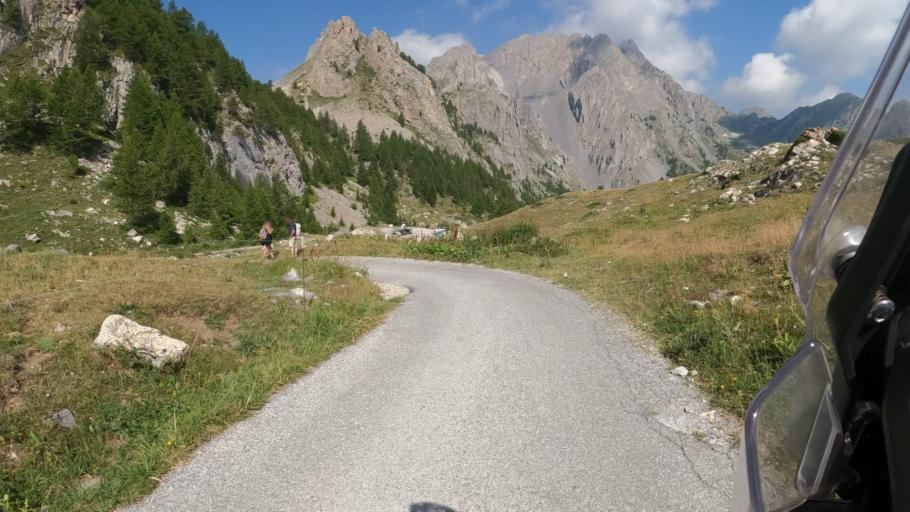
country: IT
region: Piedmont
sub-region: Provincia di Cuneo
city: Pietraporzio
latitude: 44.4049
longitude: 7.0412
